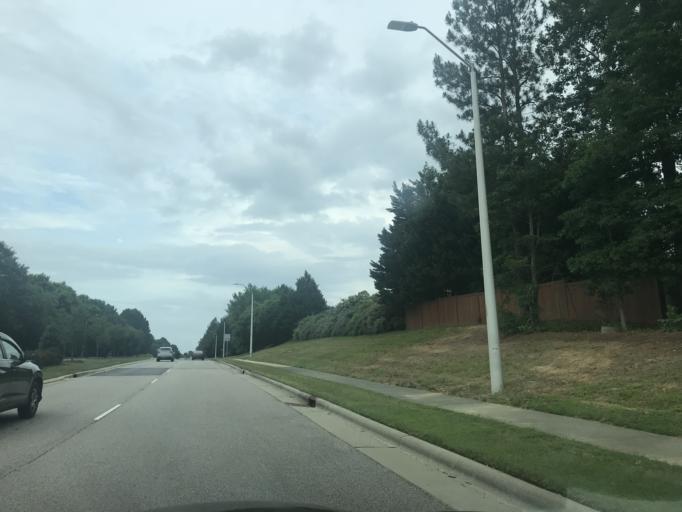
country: US
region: North Carolina
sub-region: Wake County
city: Morrisville
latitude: 35.8132
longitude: -78.8617
